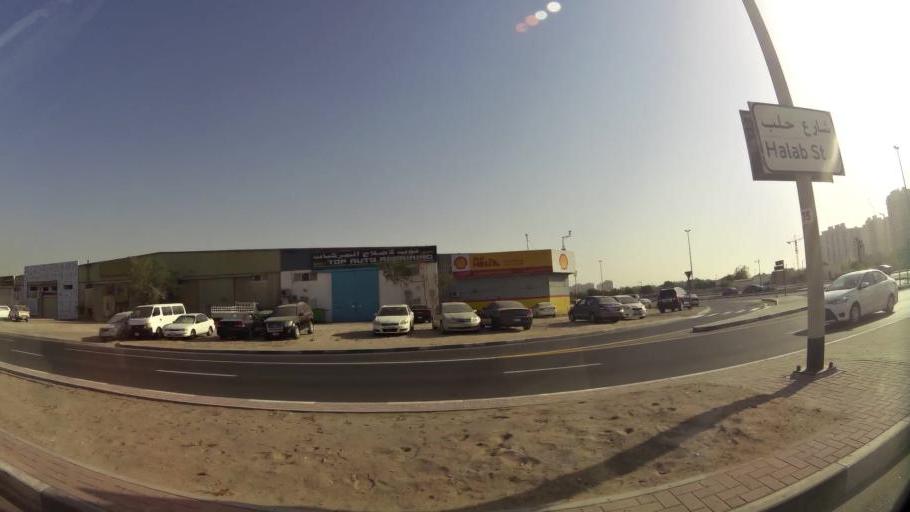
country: AE
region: Ash Shariqah
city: Sharjah
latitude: 25.2881
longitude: 55.3835
